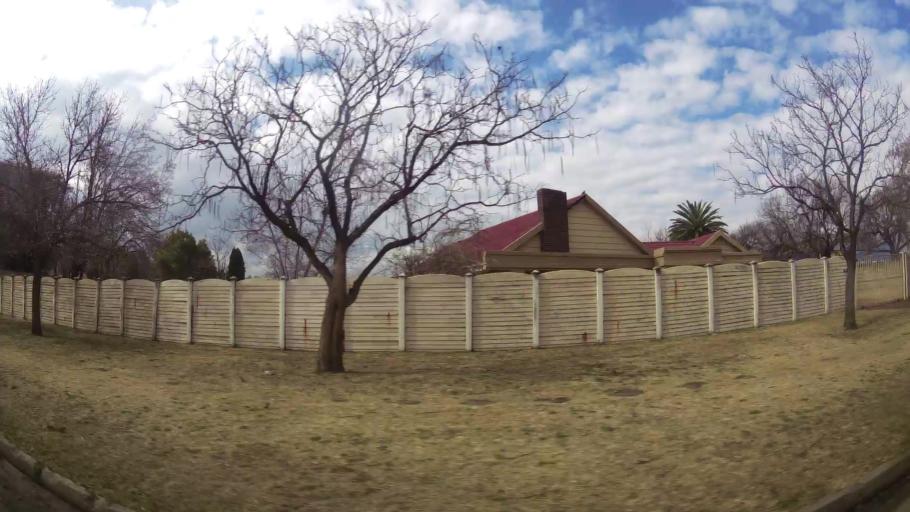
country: ZA
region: Gauteng
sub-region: Sedibeng District Municipality
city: Vereeniging
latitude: -26.6526
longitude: 27.9738
